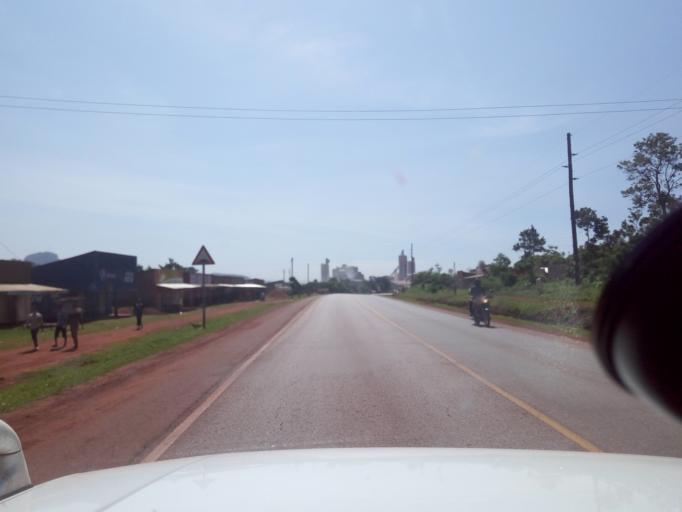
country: UG
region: Eastern Region
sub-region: Tororo District
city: Tororo
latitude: 0.6588
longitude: 34.1464
